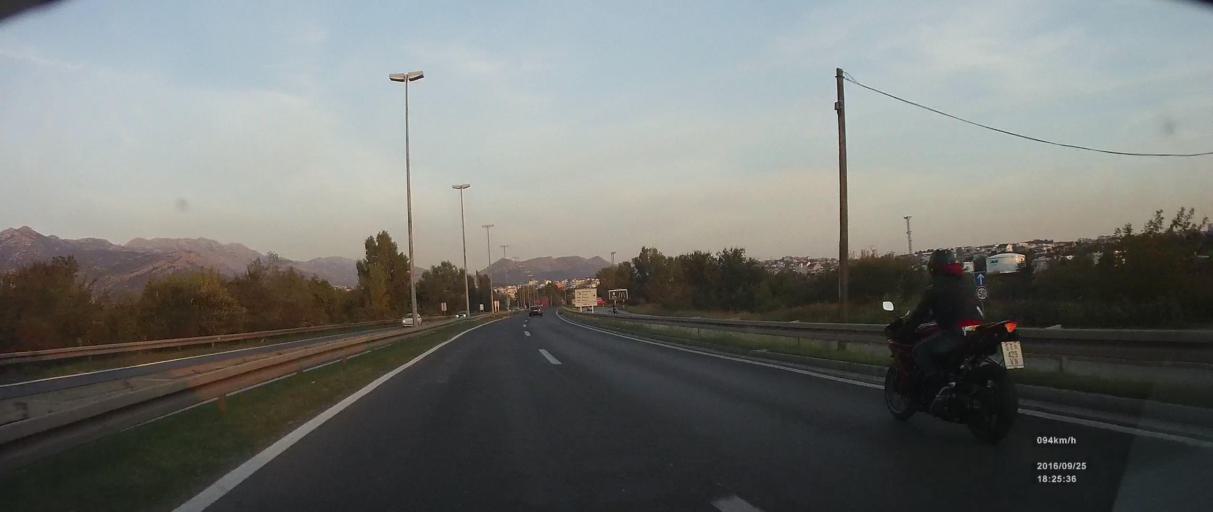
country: HR
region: Splitsko-Dalmatinska
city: Vranjic
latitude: 43.5366
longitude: 16.4773
